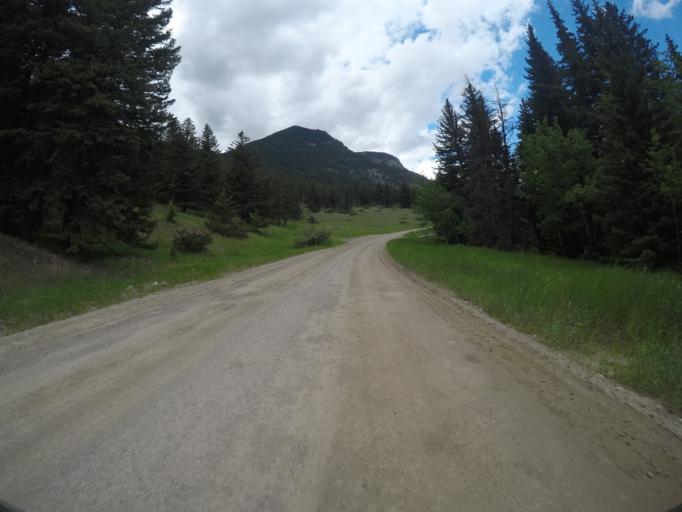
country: US
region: Montana
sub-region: Park County
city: Livingston
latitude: 45.4920
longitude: -110.2249
